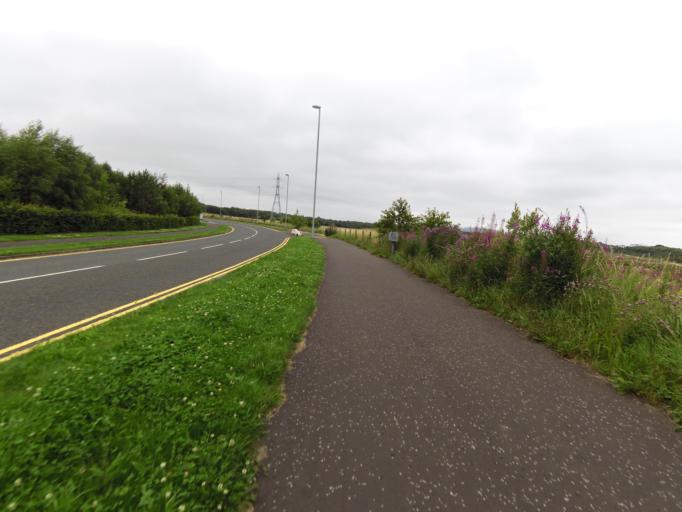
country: GB
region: Scotland
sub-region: East Lothian
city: Musselburgh
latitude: 55.9331
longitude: -3.0745
